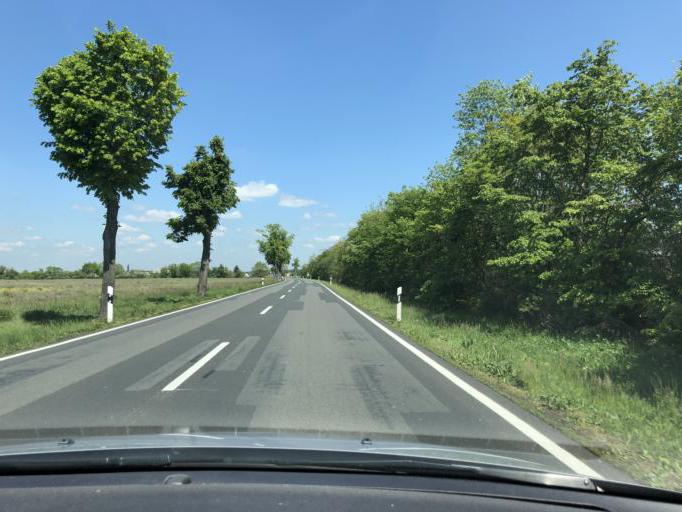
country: DE
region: Saxony
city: Arzberg
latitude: 51.6033
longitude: 13.1315
